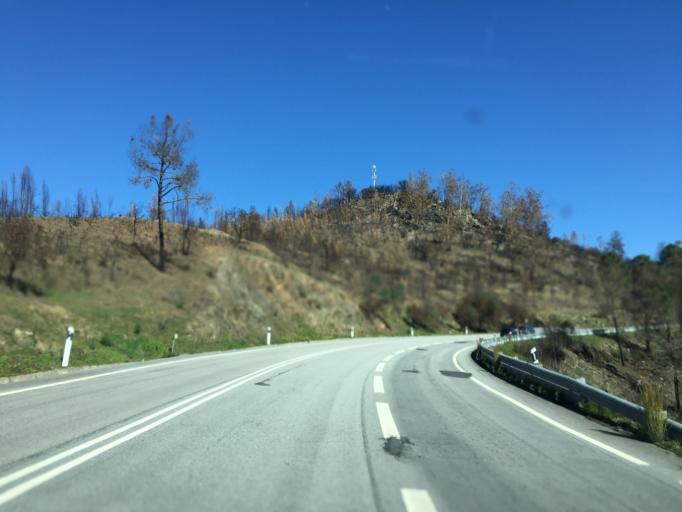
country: PT
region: Portalegre
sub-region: Nisa
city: Nisa
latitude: 39.5489
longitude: -7.7975
